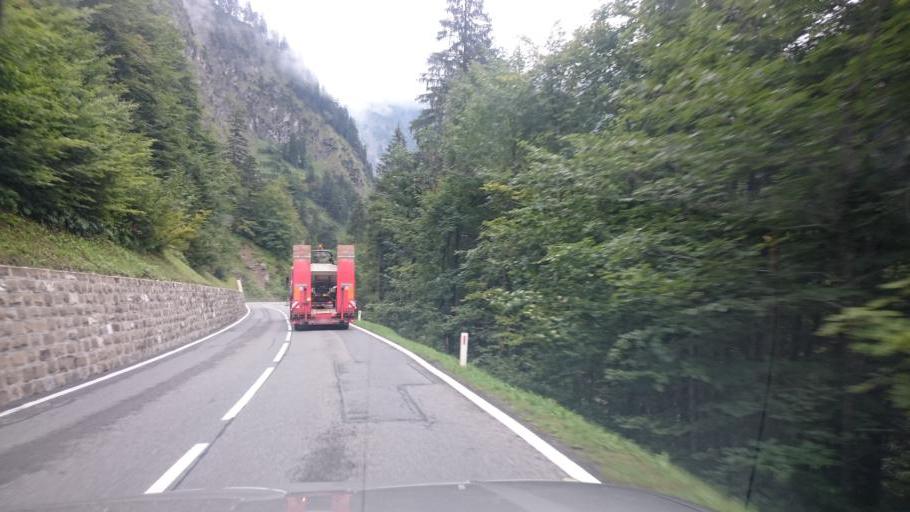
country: AT
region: Vorarlberg
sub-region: Politischer Bezirk Bregenz
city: Schroecken
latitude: 47.2737
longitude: 10.0640
